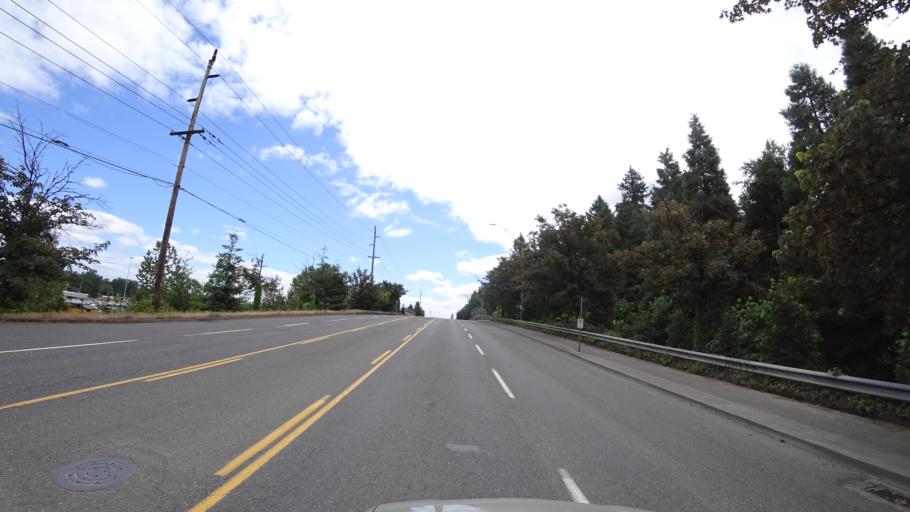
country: US
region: Oregon
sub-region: Washington County
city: West Haven
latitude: 45.6065
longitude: -122.7559
